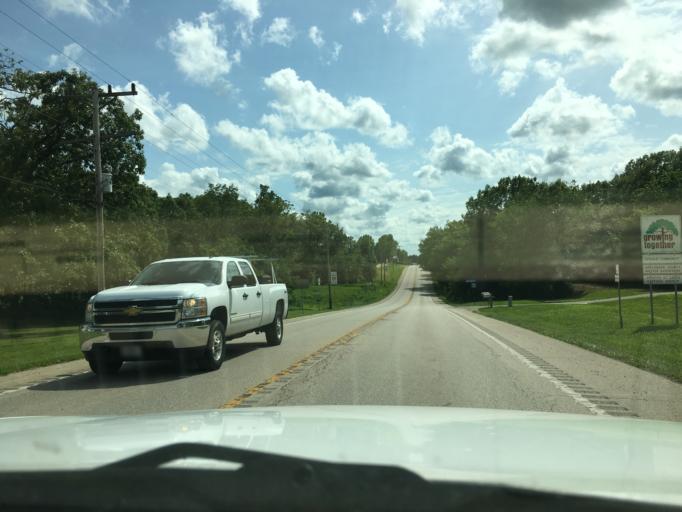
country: US
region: Missouri
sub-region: Franklin County
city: Gerald
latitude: 38.4078
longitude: -91.3206
